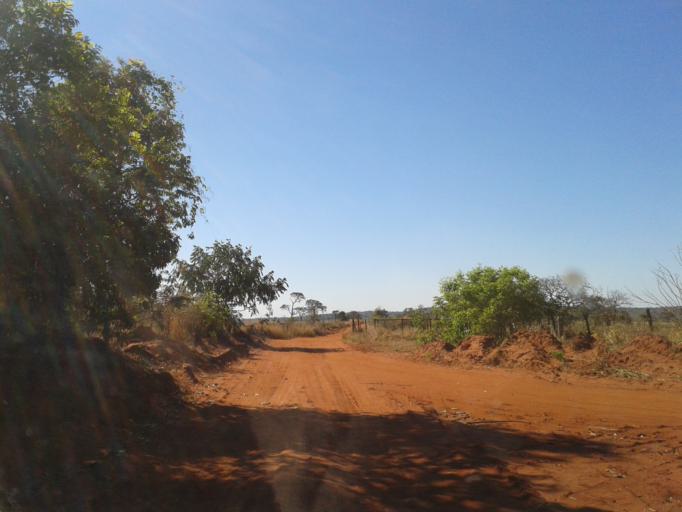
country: BR
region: Minas Gerais
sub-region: Ituiutaba
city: Ituiutaba
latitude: -19.0725
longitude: -49.3378
